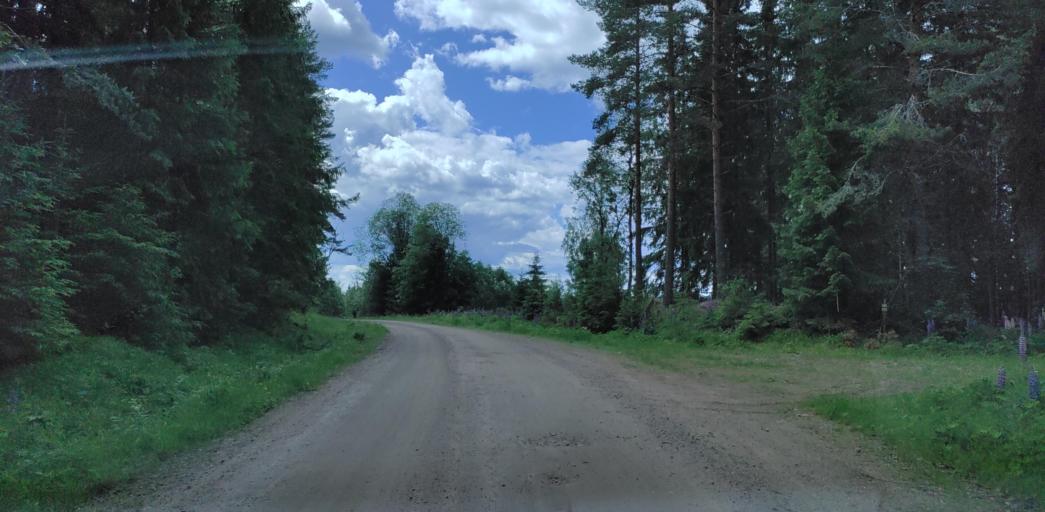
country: SE
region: Vaermland
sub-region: Hagfors Kommun
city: Ekshaerad
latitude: 60.0851
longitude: 13.3182
